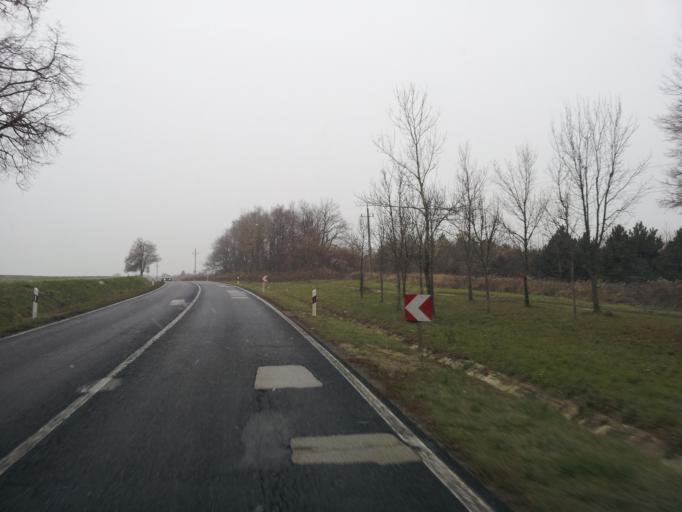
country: HU
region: Veszprem
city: Herend
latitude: 47.1427
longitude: 17.7069
